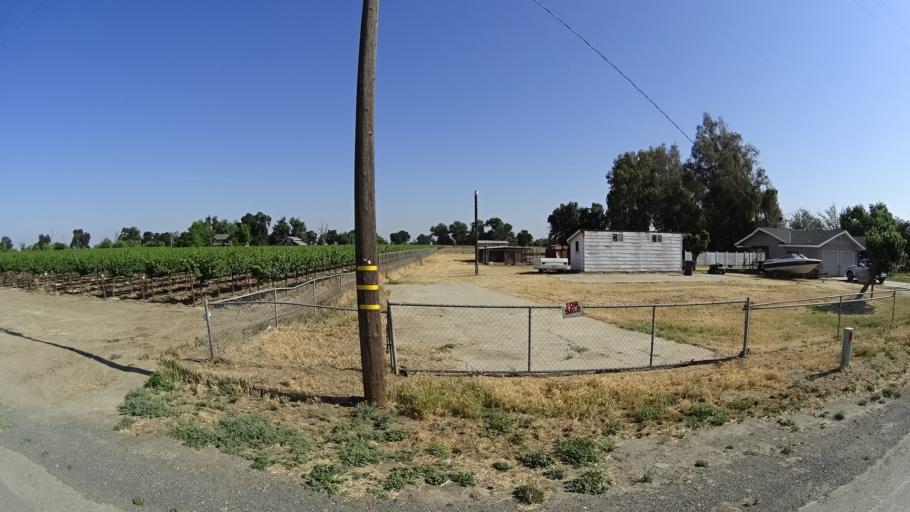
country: US
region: California
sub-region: Kings County
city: Lemoore
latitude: 36.3439
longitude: -119.8555
